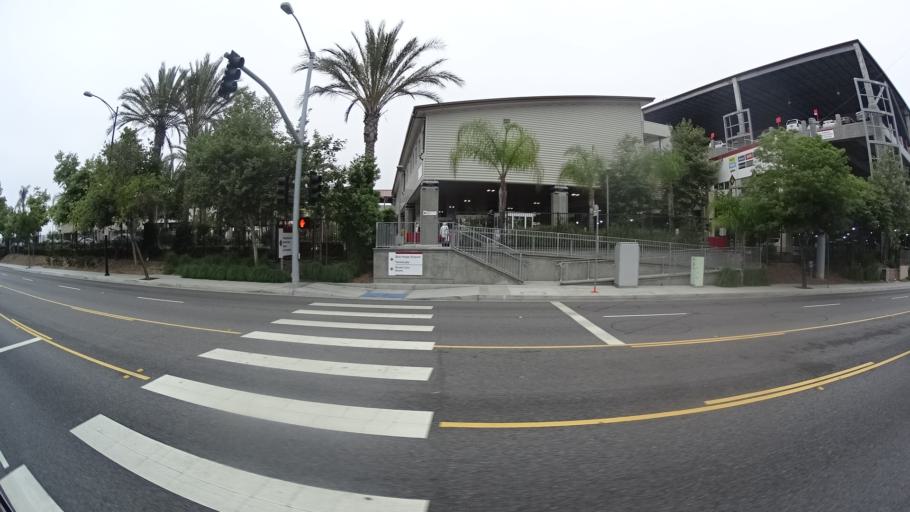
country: US
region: California
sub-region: Los Angeles County
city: North Hollywood
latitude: 34.1927
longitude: -118.3517
